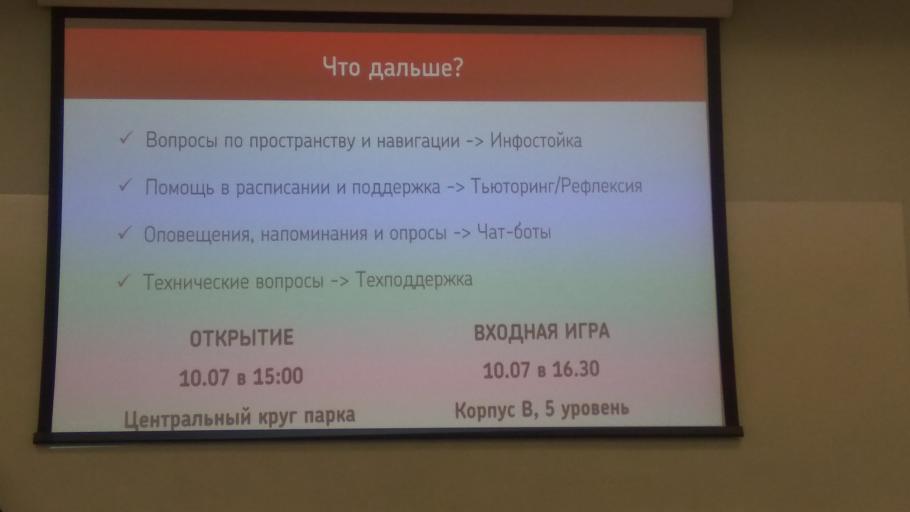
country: RU
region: Primorskiy
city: Russkiy
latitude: 43.0257
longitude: 131.8915
